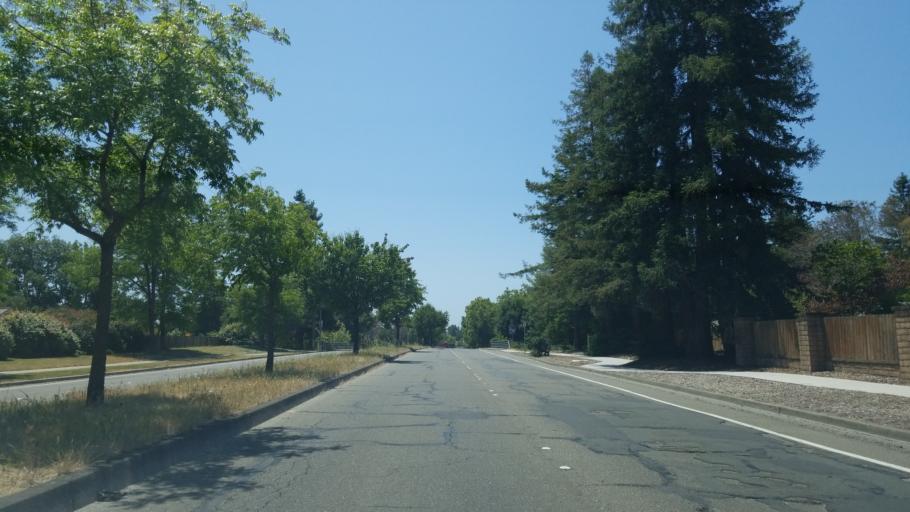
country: US
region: California
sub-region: Sonoma County
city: Roseland
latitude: 38.4429
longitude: -122.7697
